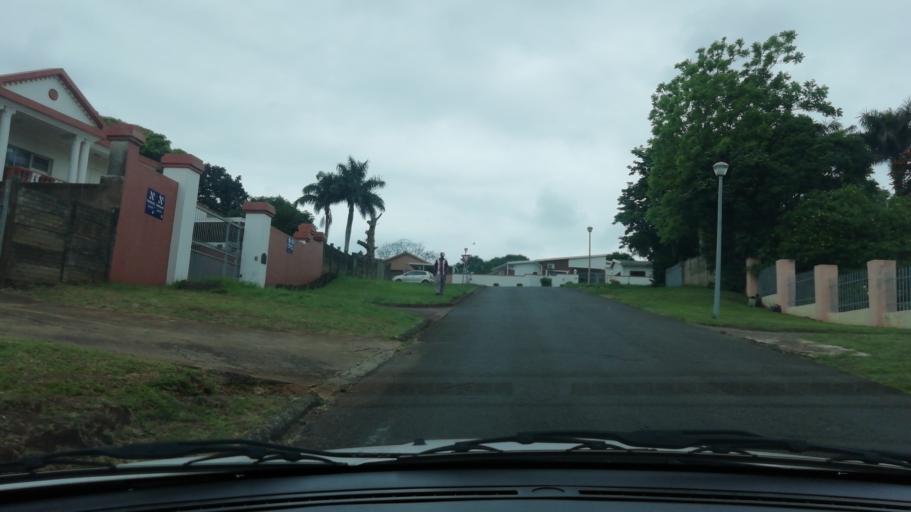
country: ZA
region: KwaZulu-Natal
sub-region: uThungulu District Municipality
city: Empangeni
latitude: -28.7583
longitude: 31.8869
